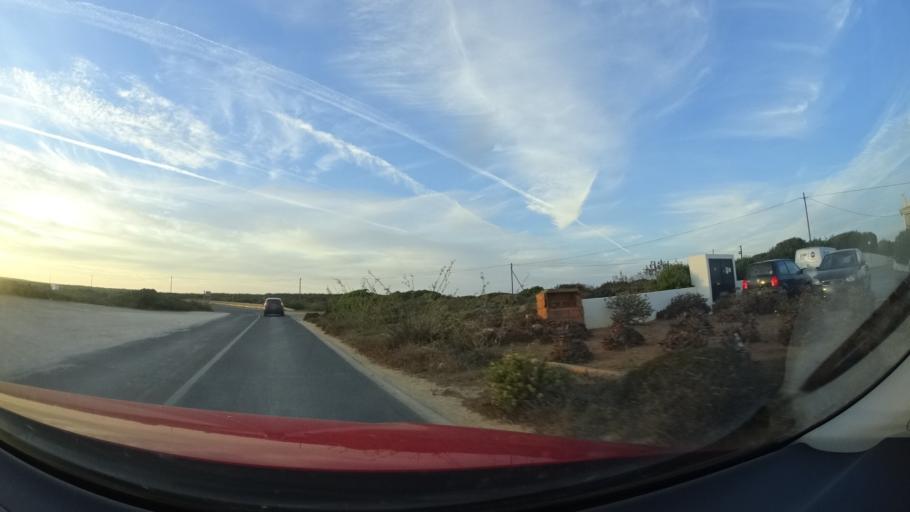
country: PT
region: Faro
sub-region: Vila do Bispo
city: Sagres
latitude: 37.0270
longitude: -8.9635
